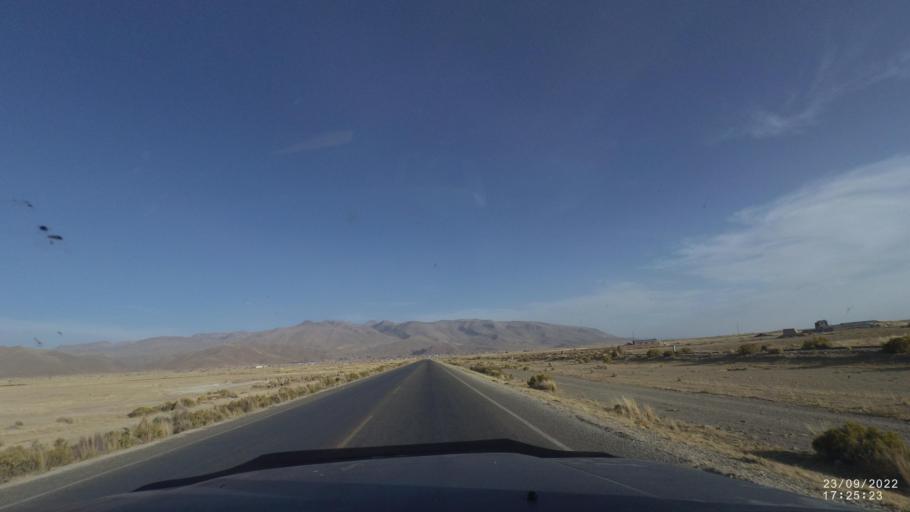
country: BO
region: Oruro
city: Challapata
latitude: -18.8698
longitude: -66.7980
